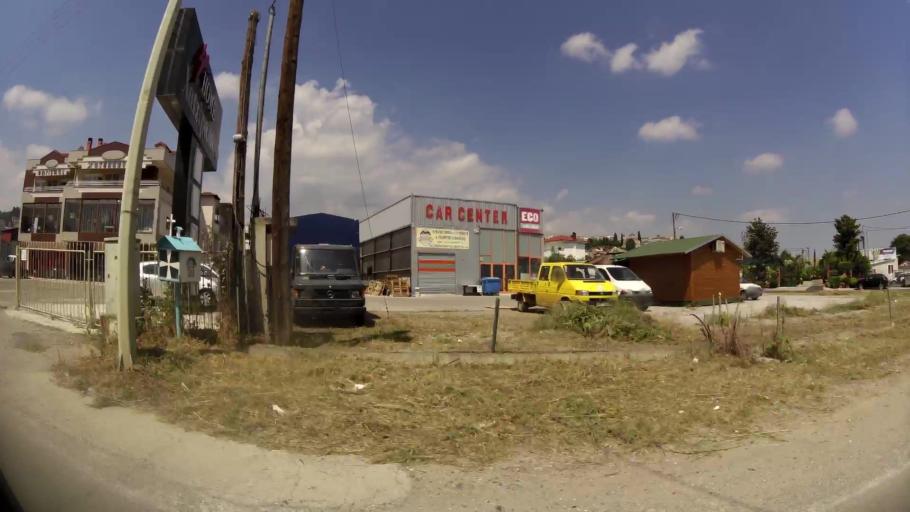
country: GR
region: Central Macedonia
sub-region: Nomos Imathias
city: Veroia
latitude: 40.5219
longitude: 22.2138
